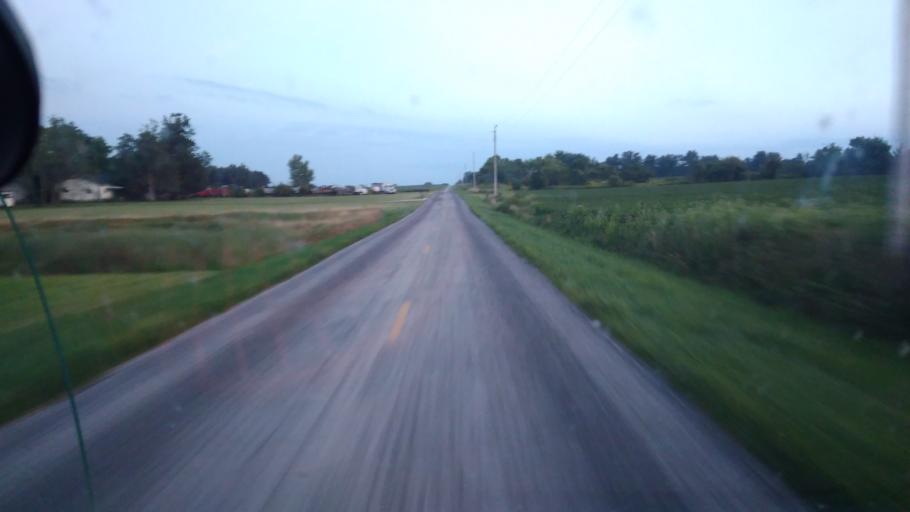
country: US
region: Ohio
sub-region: Hardin County
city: Kenton
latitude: 40.6380
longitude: -83.4576
